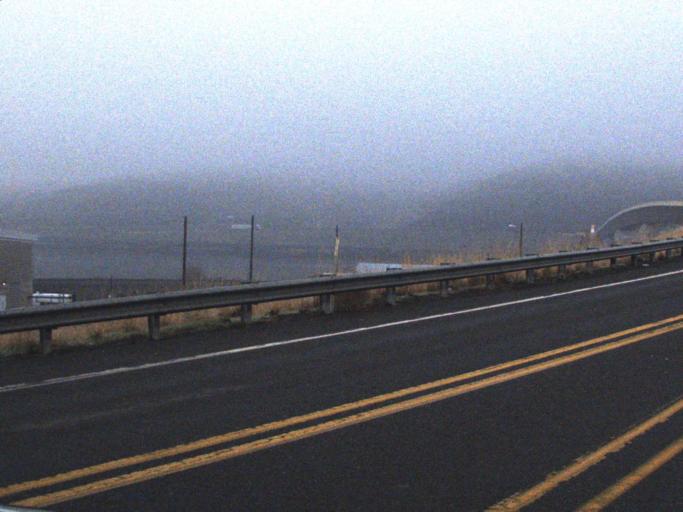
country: US
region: Washington
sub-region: Asotin County
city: West Clarkston-Highland
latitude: 46.4218
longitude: -117.0695
